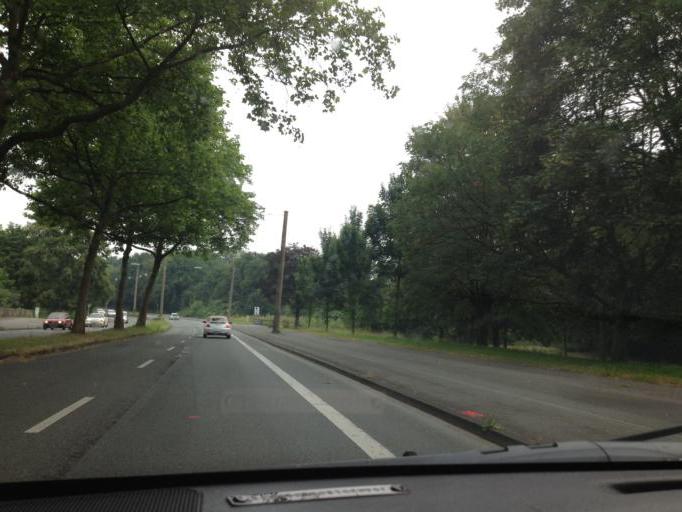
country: DE
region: North Rhine-Westphalia
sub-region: Regierungsbezirk Arnsberg
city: Dortmund
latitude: 51.4856
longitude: 7.4601
